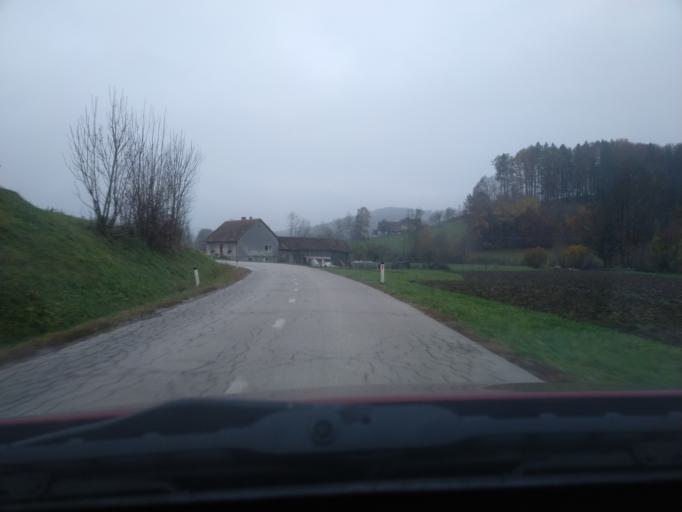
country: SI
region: Kungota
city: Zgornja Kungota
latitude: 46.6582
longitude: 15.6117
